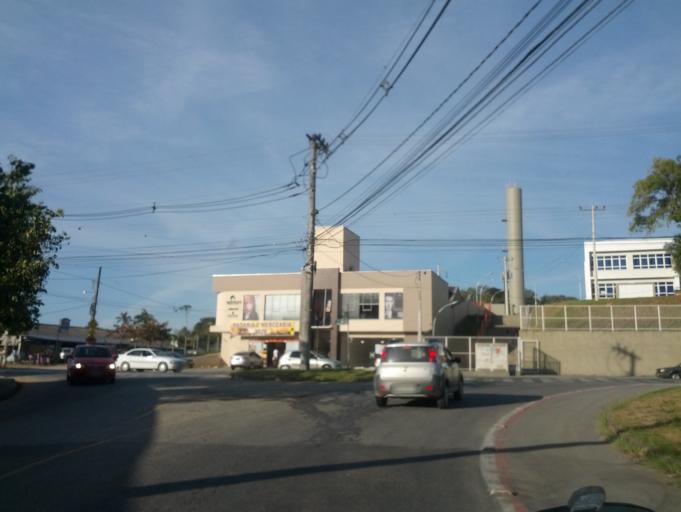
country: BR
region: Santa Catarina
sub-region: Indaial
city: Indaial
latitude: -26.9007
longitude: -49.1497
